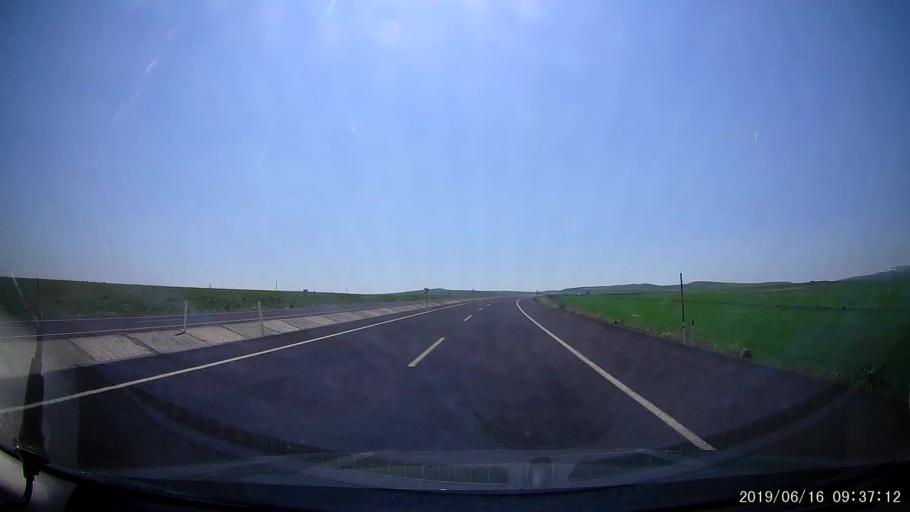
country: TR
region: Kars
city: Kars
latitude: 40.5543
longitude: 43.1894
